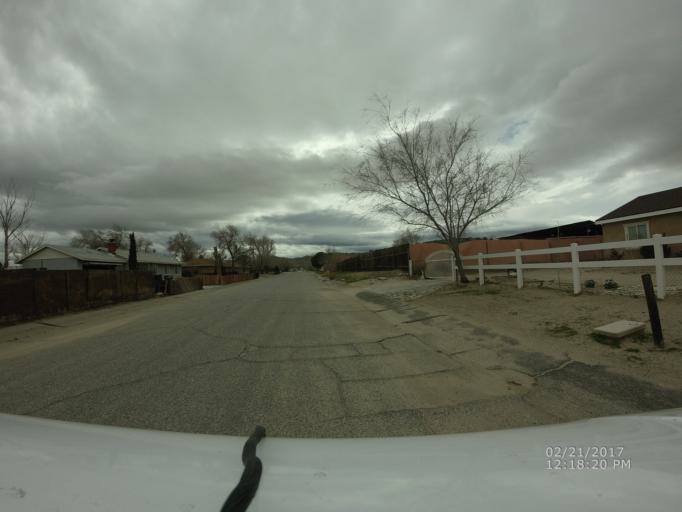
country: US
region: California
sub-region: Los Angeles County
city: Lake Los Angeles
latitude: 34.6338
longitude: -117.8556
